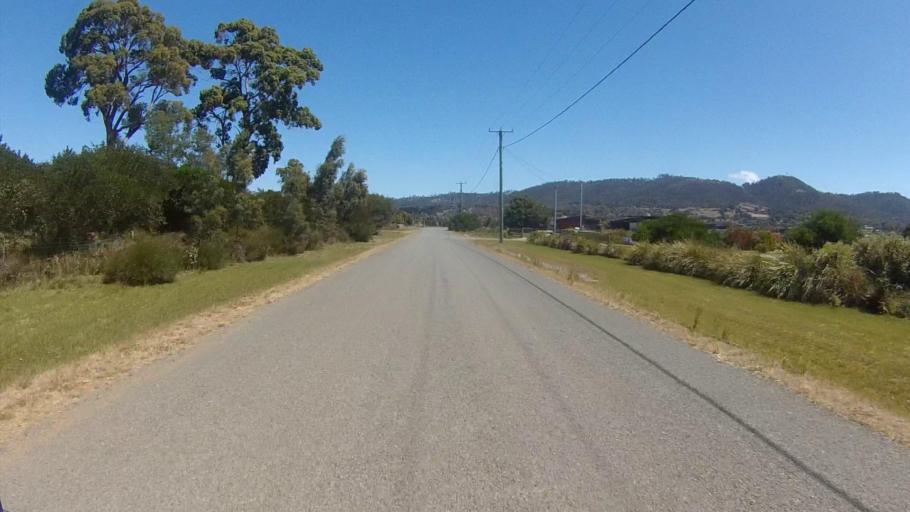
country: AU
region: Tasmania
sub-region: Clarence
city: Seven Mile Beach
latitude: -42.8502
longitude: 147.4926
